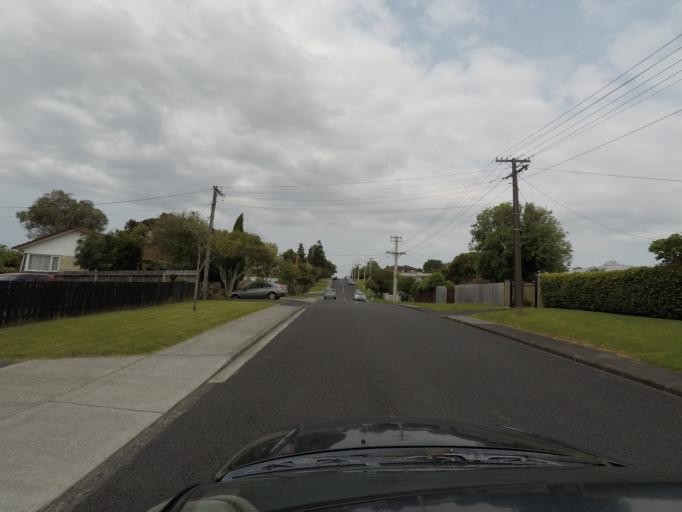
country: NZ
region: Auckland
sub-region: Auckland
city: Rosebank
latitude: -36.8397
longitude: 174.6347
